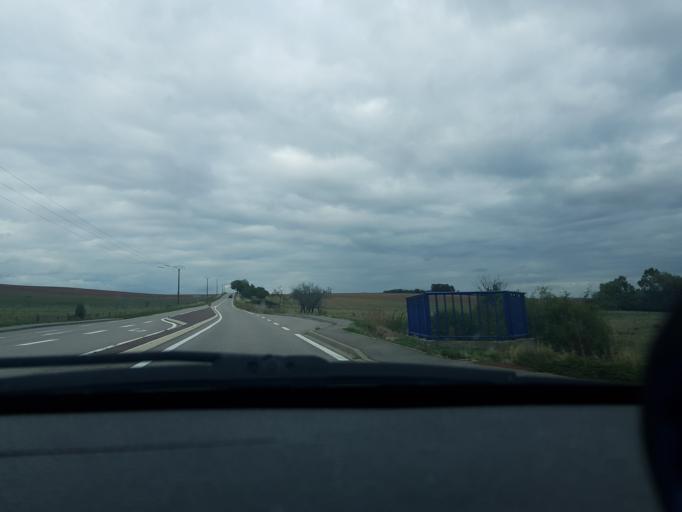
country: FR
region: Lorraine
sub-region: Departement de la Moselle
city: Chateau-Salins
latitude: 48.8623
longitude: 6.5248
